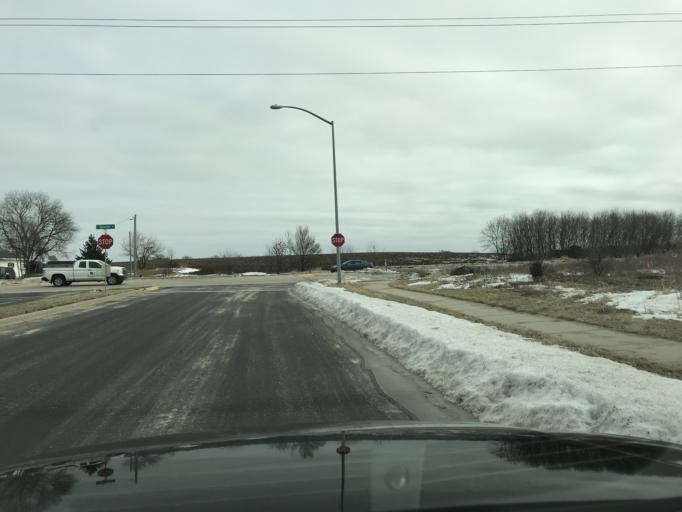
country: US
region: Wisconsin
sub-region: Dane County
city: Cottage Grove
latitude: 43.1016
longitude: -89.2673
